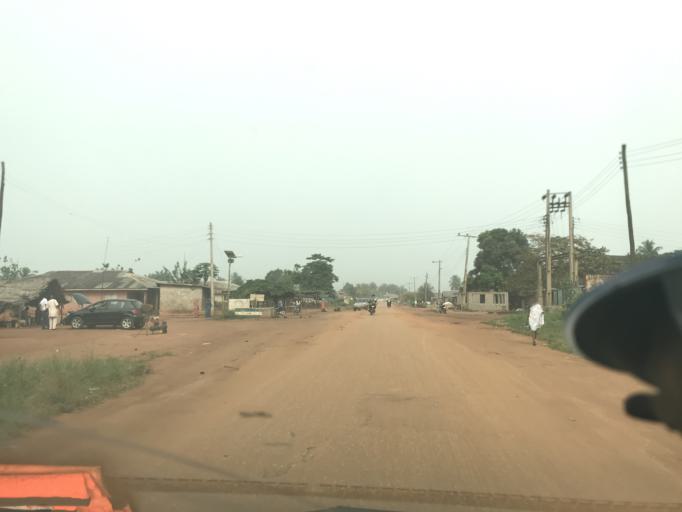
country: NG
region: Ogun
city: Ado Odo
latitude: 6.5767
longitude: 2.9369
